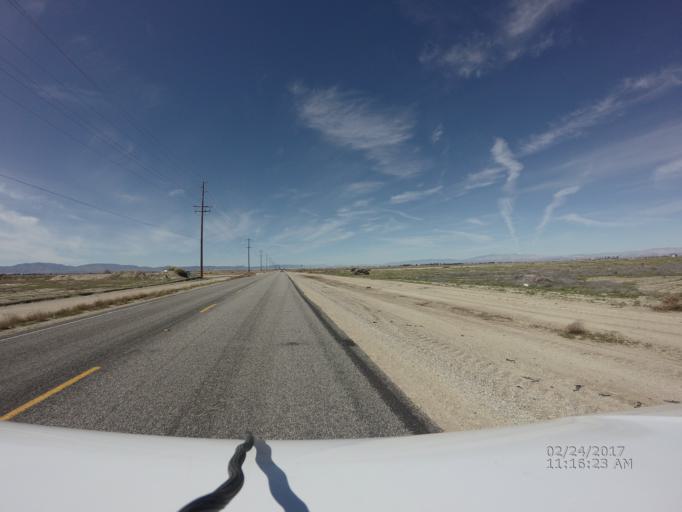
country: US
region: California
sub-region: Los Angeles County
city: Lancaster
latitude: 34.6900
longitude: -118.0311
